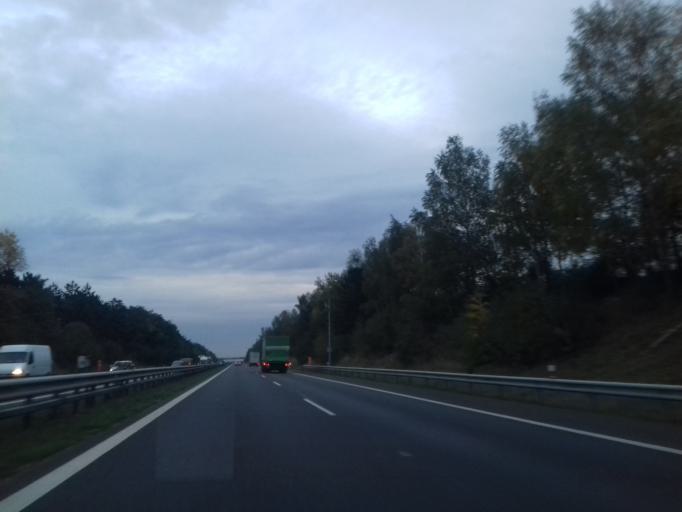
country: CZ
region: Central Bohemia
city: Nehvizdy
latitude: 50.1275
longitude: 14.7388
